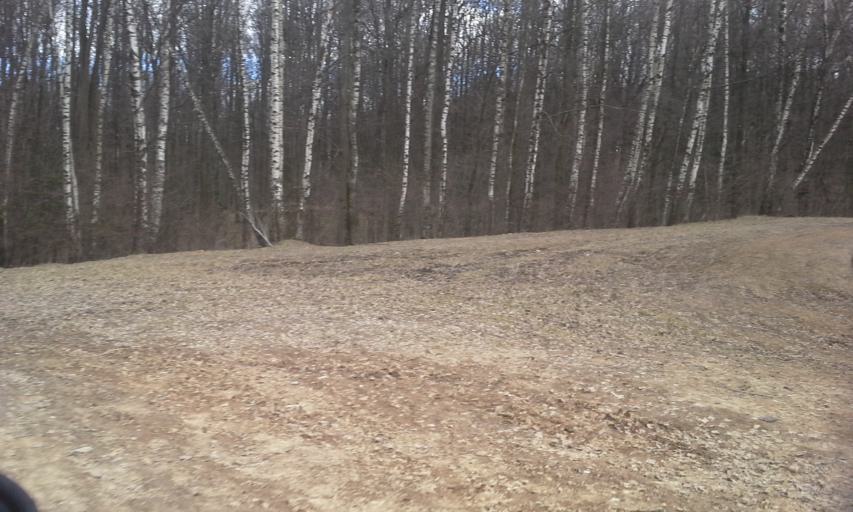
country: RU
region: Moscow
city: Yasenevo
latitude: 55.5827
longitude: 37.5458
